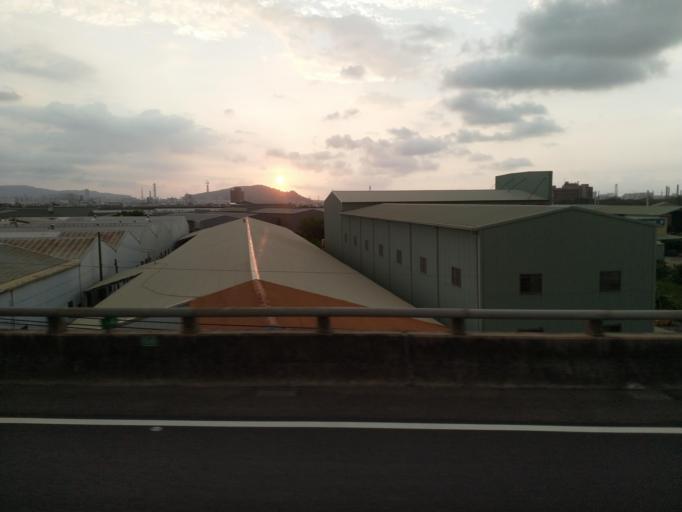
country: TW
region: Taiwan
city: Fengshan
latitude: 22.7109
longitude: 120.3602
